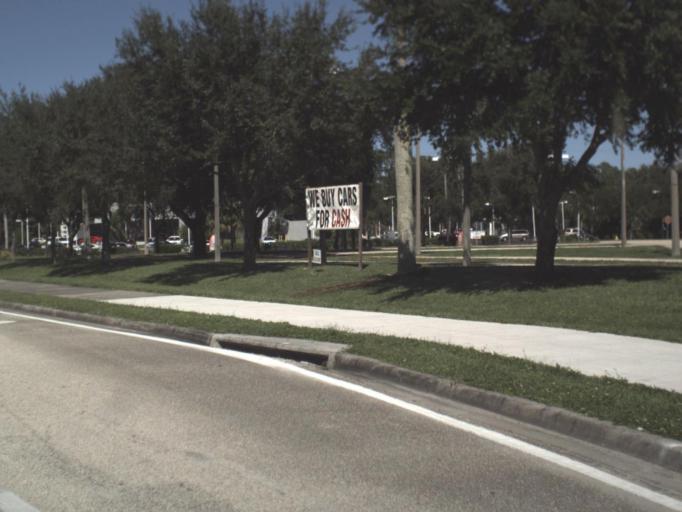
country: US
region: Florida
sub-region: Lee County
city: Villas
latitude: 26.5145
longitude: -81.8644
